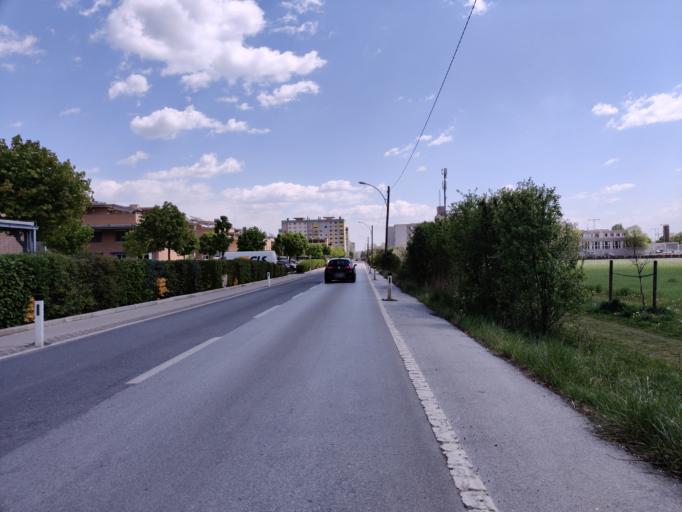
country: AT
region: Styria
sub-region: Graz Stadt
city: Wetzelsdorf
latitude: 47.0466
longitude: 15.3902
